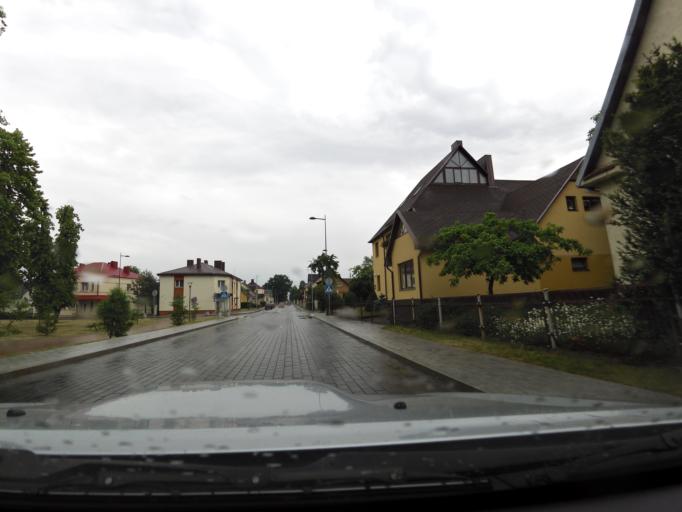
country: LT
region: Marijampoles apskritis
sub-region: Marijampole Municipality
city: Marijampole
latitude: 54.5523
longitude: 23.3451
